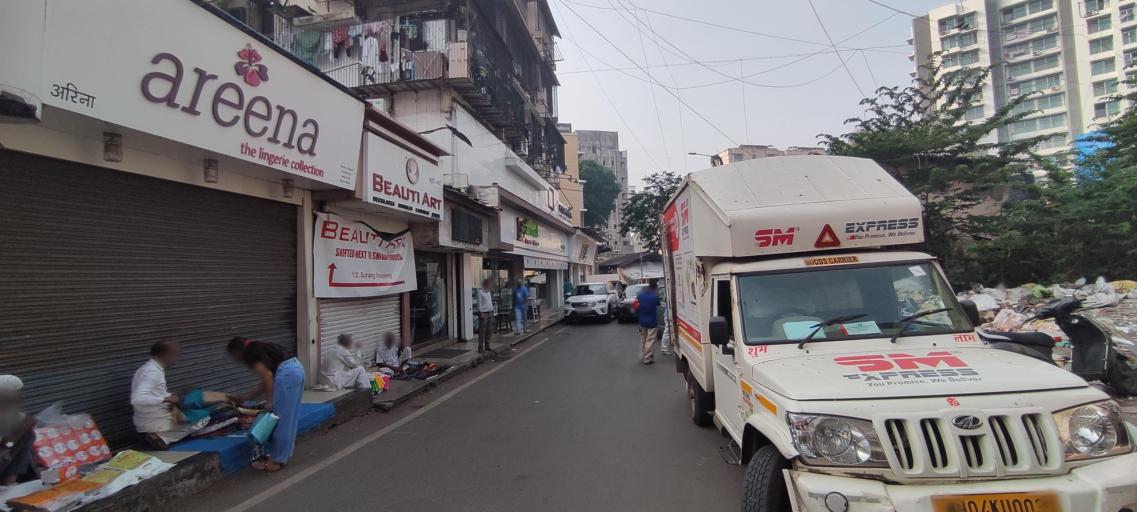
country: IN
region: Maharashtra
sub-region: Mumbai Suburban
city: Mumbai
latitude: 19.0816
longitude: 72.8409
